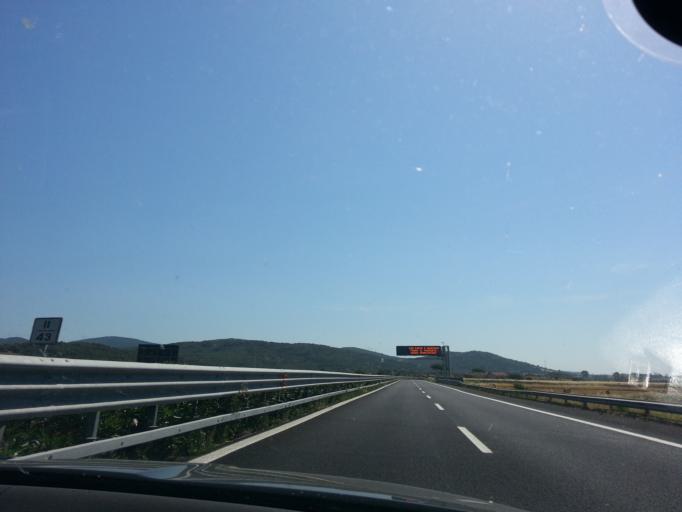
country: IT
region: Latium
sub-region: Citta metropolitana di Roma Capitale
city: Santa Marinella
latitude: 42.0438
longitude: 11.9189
